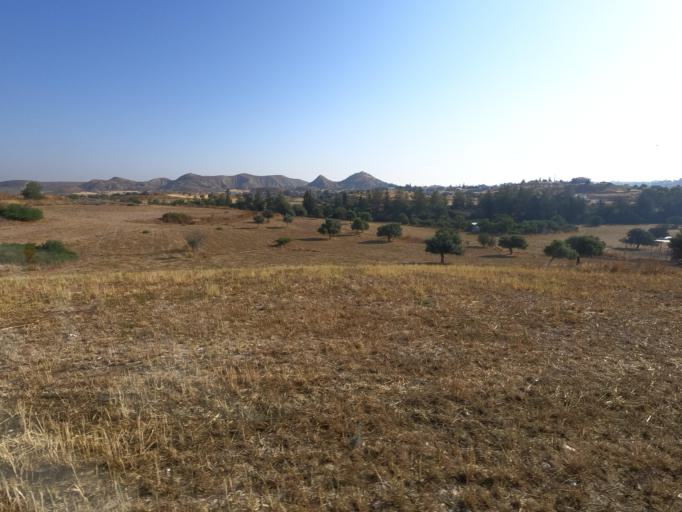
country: CY
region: Lefkosia
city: Lympia
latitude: 34.9910
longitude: 33.4520
